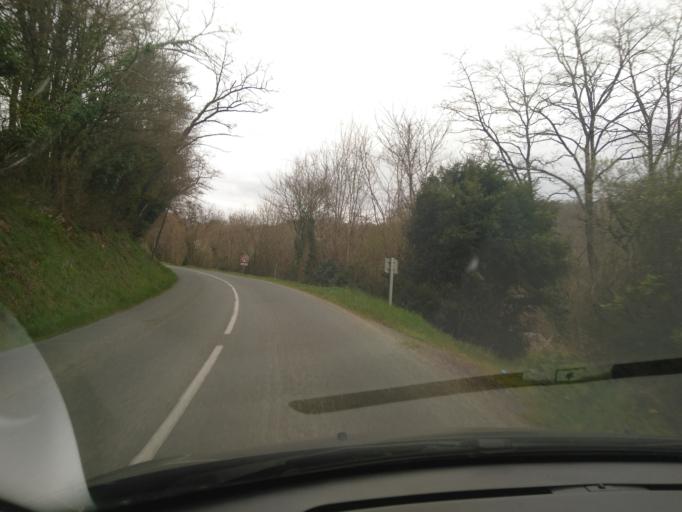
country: FR
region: Aquitaine
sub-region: Departement du Lot-et-Garonne
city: Foulayronnes
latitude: 44.2281
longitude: 0.6240
